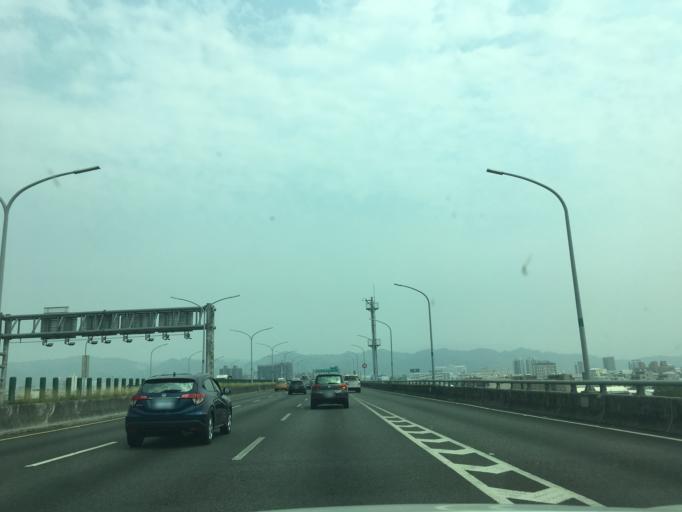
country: TW
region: Taiwan
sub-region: Taichung City
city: Taichung
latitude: 24.2010
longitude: 120.6919
